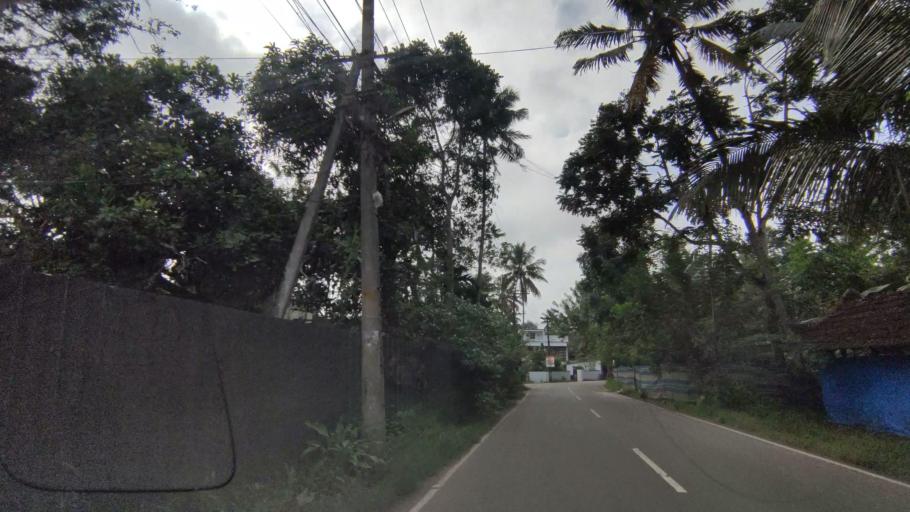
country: IN
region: Kerala
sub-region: Alappuzha
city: Shertallai
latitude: 9.6399
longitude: 76.3606
